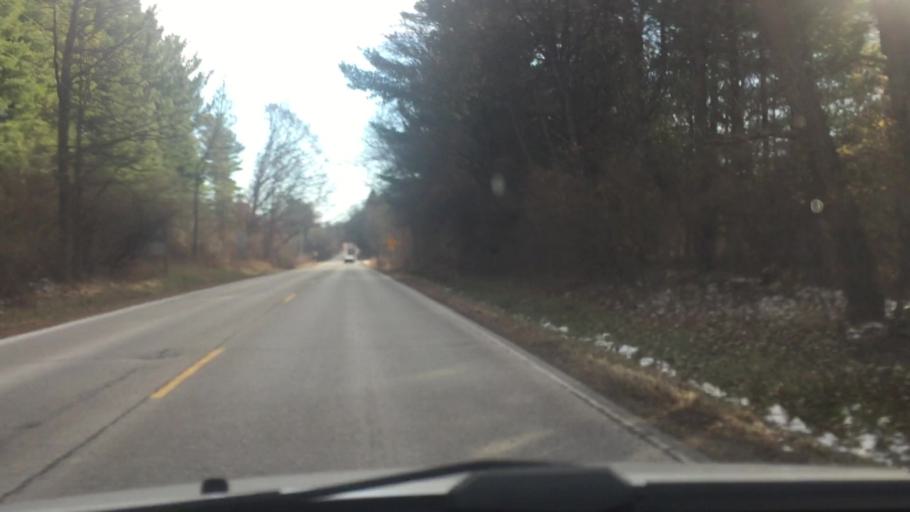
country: US
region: Wisconsin
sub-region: Waukesha County
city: Delafield
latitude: 43.0398
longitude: -88.4043
